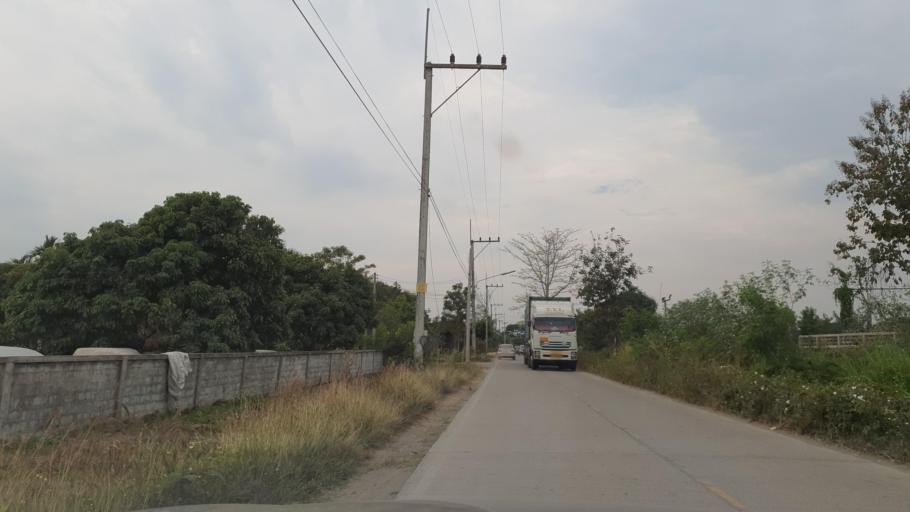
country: TH
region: Chiang Mai
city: Hang Dong
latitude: 18.6862
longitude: 98.9365
